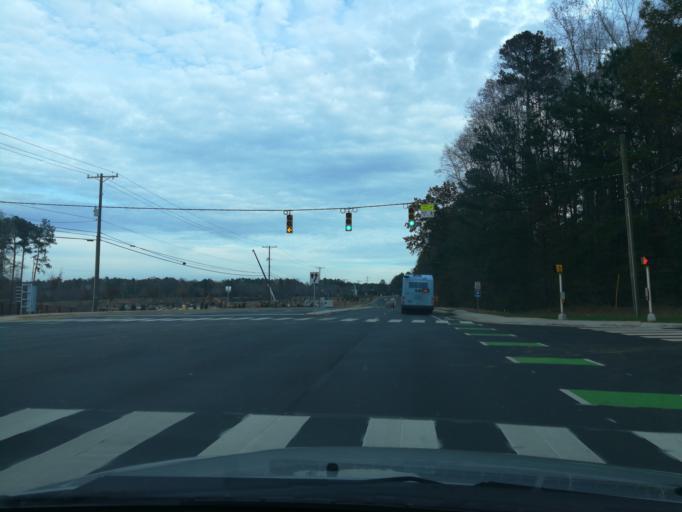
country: US
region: North Carolina
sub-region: Orange County
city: Chapel Hill
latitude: 35.9694
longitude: -79.0666
